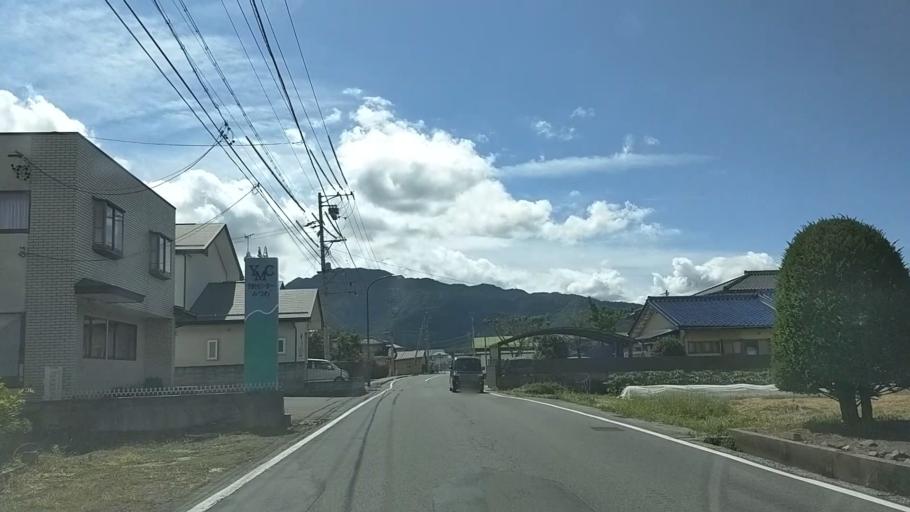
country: JP
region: Nagano
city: Suzaka
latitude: 36.6158
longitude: 138.2509
